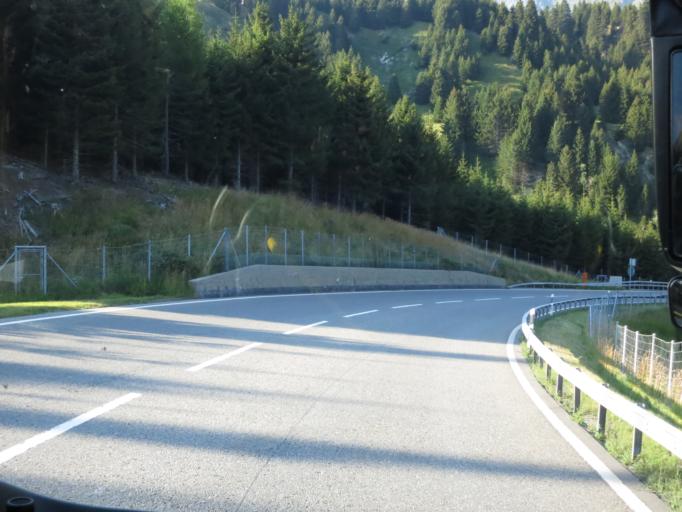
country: CH
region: Grisons
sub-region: Moesa District
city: Mesocco
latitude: 46.4379
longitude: 9.2103
